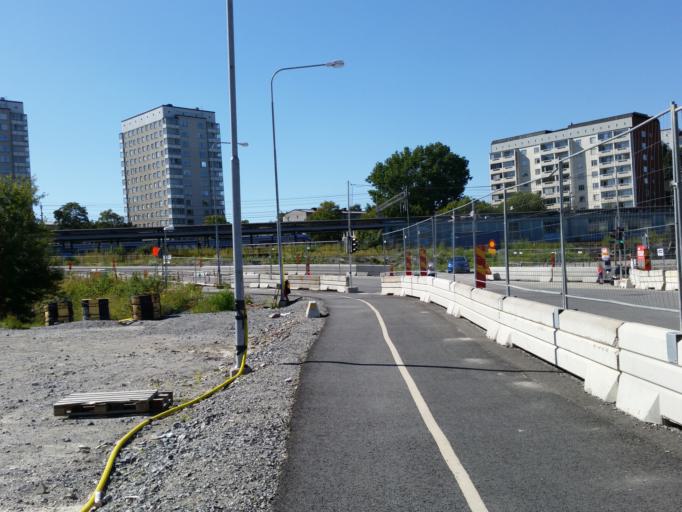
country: SE
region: Stockholm
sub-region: Solna Kommun
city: Solna
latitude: 59.3810
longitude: 18.0025
